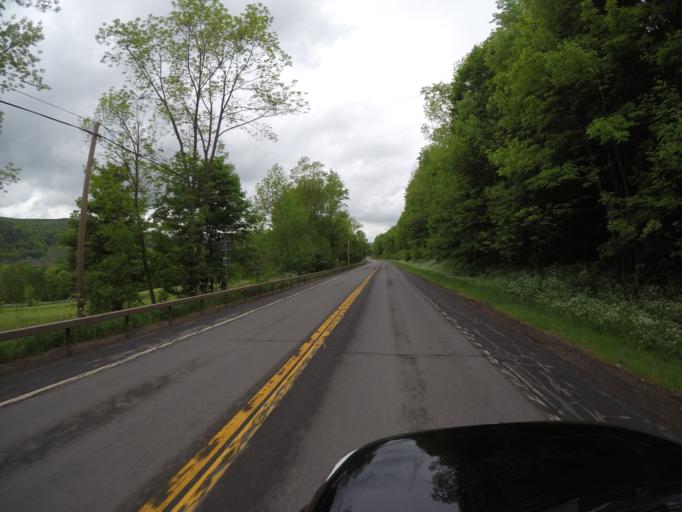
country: US
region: New York
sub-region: Delaware County
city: Delhi
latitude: 42.2588
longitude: -74.9216
